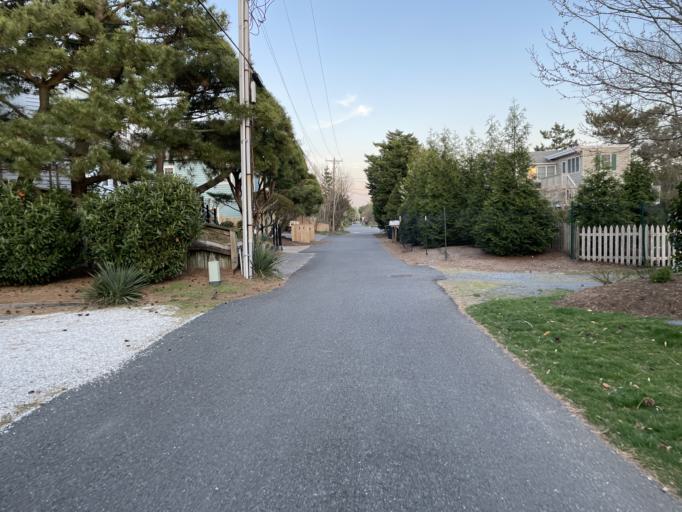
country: US
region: Delaware
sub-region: Sussex County
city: Lewes
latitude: 38.7856
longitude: -75.1495
